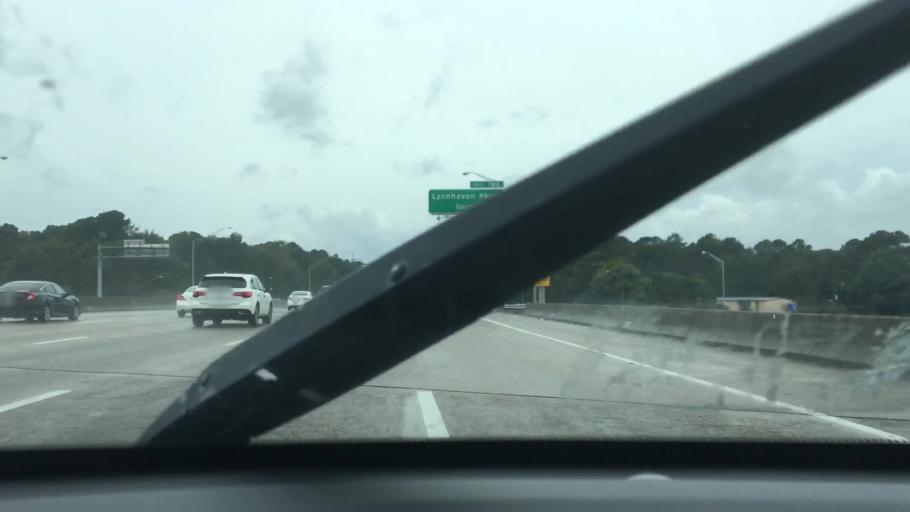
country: US
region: Virginia
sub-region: City of Virginia Beach
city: Virginia Beach
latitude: 36.8361
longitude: -76.0659
